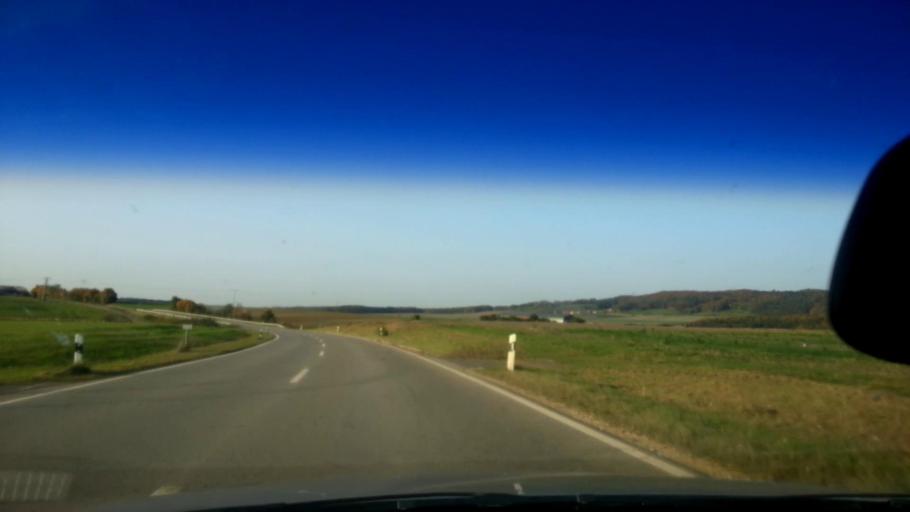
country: DE
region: Bavaria
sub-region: Upper Franconia
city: Schesslitz
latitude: 49.9951
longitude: 11.0237
